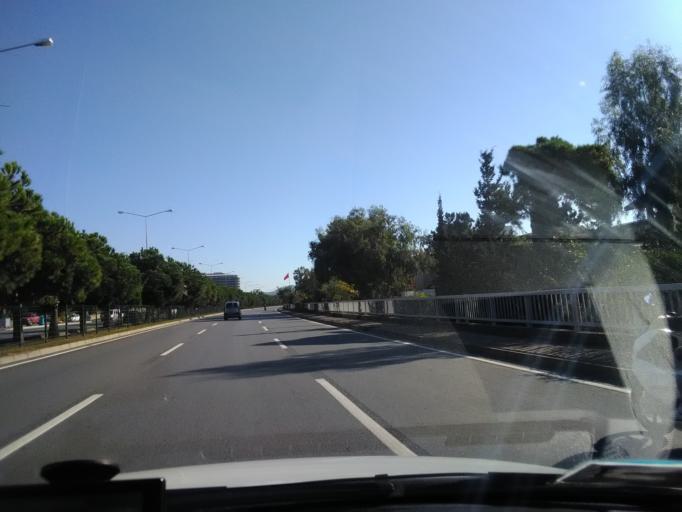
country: TR
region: Antalya
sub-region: Alanya
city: Mahmutlar
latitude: 36.5212
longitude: 32.0567
